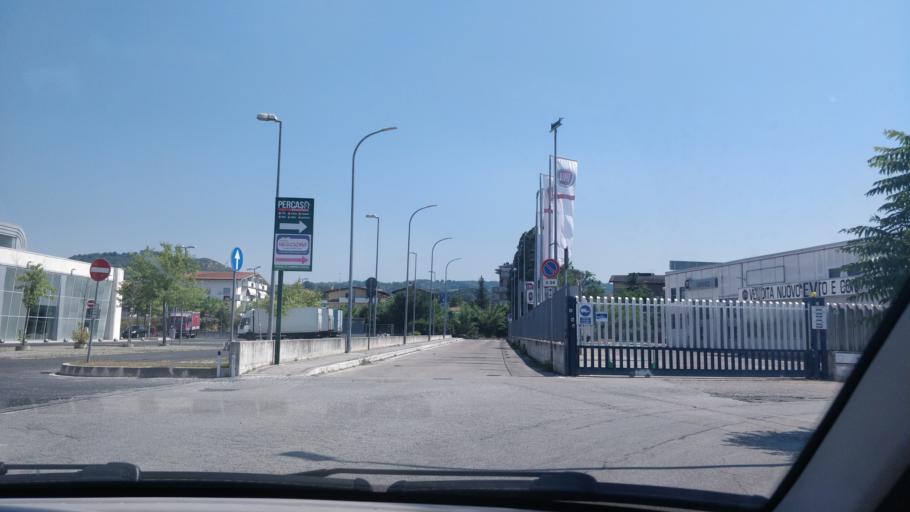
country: IT
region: Abruzzo
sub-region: Provincia di Chieti
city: Sambuceto
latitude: 42.4153
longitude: 14.1724
